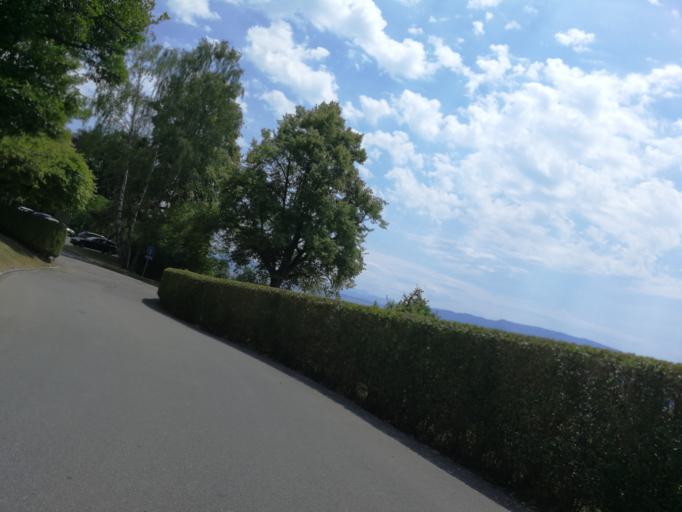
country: CH
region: Zurich
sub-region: Bezirk Meilen
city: Uetikon / Grossdorf
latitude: 47.2665
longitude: 8.6796
